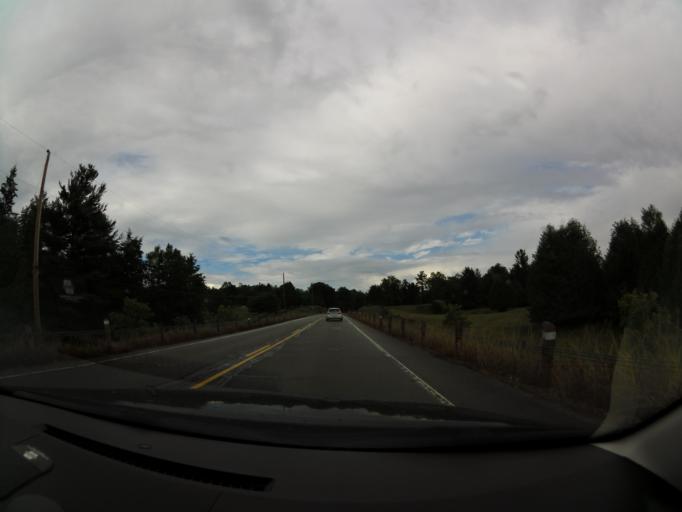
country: CA
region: Ontario
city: Carleton Place
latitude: 45.1079
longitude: -76.3795
